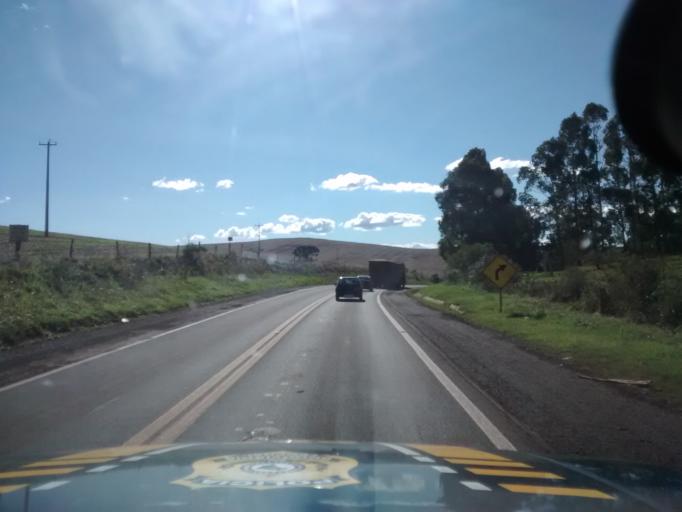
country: BR
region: Rio Grande do Sul
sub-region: Lagoa Vermelha
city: Lagoa Vermelha
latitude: -28.2866
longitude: -51.4646
